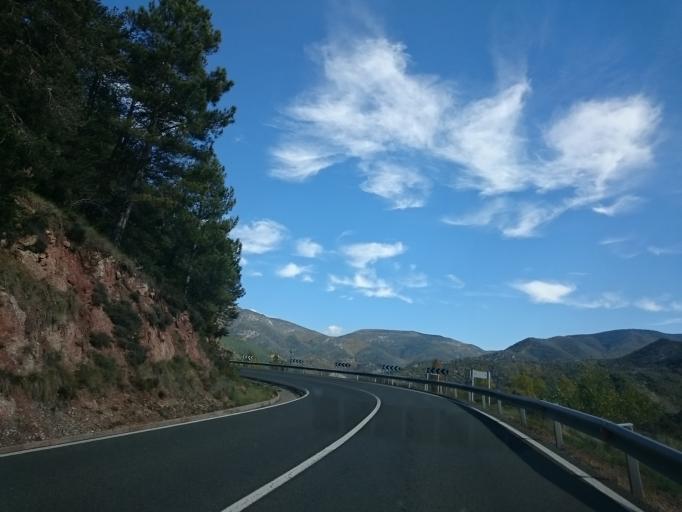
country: ES
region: Aragon
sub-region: Provincia de Huesca
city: Sopeira
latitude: 42.3370
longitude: 0.7376
